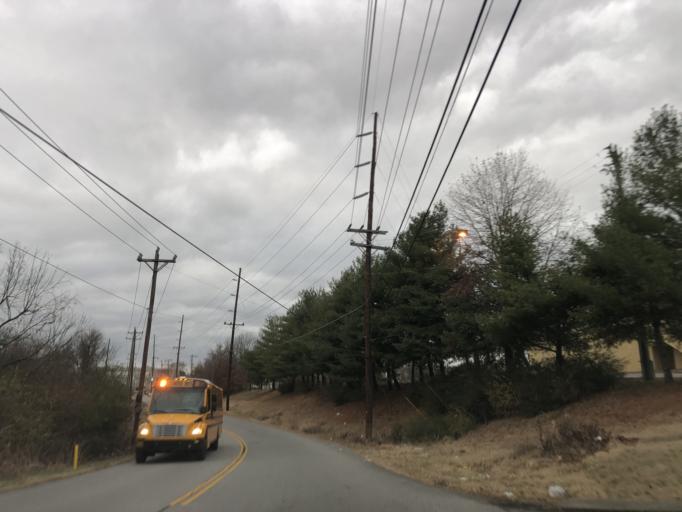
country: US
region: Tennessee
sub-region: Davidson County
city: Goodlettsville
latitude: 36.2950
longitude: -86.6941
